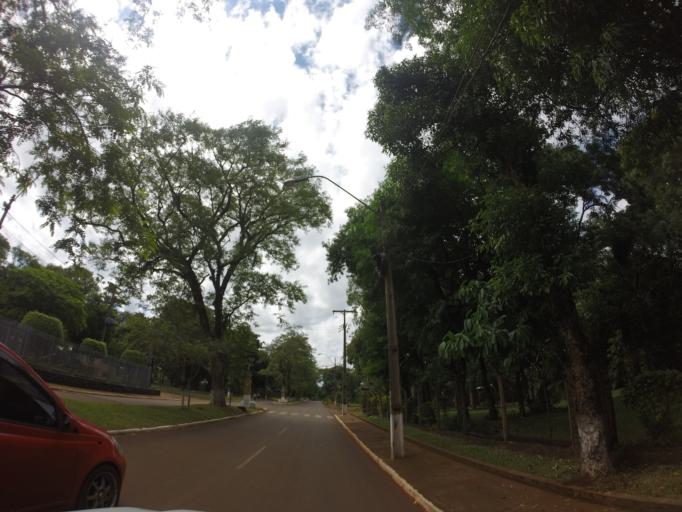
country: PY
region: Alto Parana
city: Ciudad del Este
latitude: -25.4125
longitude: -54.6376
